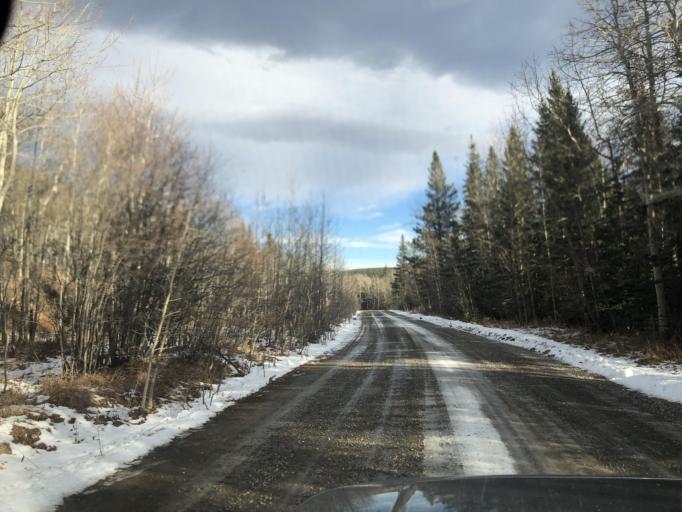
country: CA
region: Alberta
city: Cochrane
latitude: 51.0229
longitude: -114.8876
